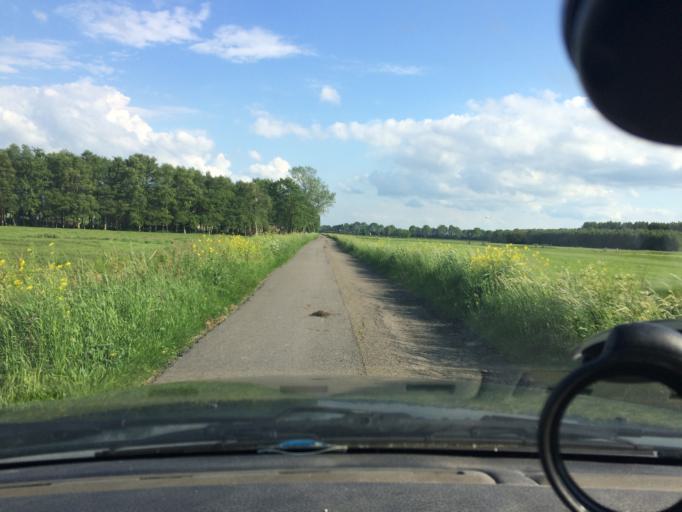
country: NL
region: North Holland
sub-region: Gemeente Haarlem
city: Haarlem
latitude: 52.3942
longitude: 4.7106
